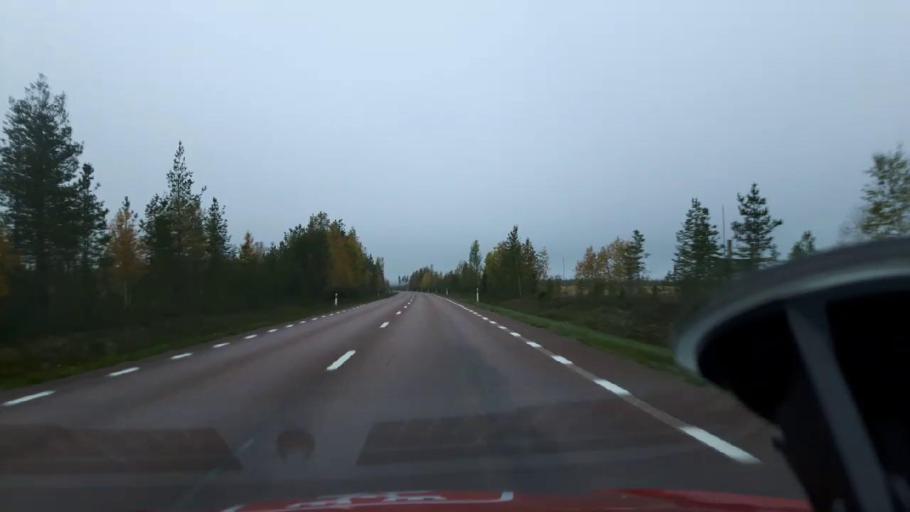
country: SE
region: Jaemtland
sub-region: Bergs Kommun
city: Hoverberg
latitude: 62.5267
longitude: 14.4469
